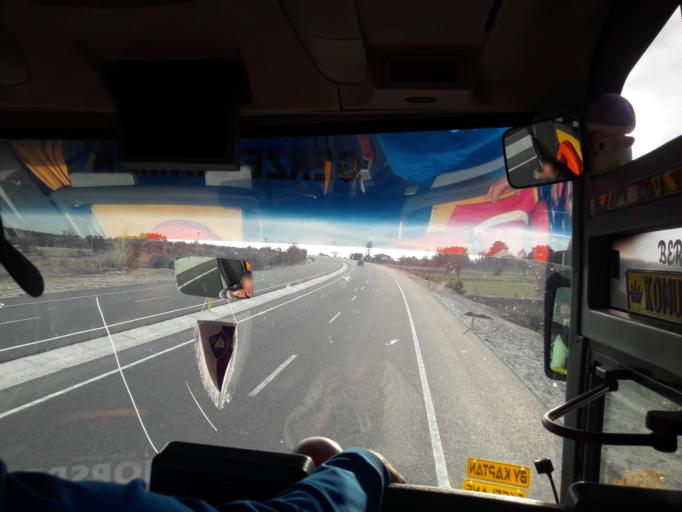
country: TR
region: Cankiri
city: Ilgaz
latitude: 40.8584
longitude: 33.6158
